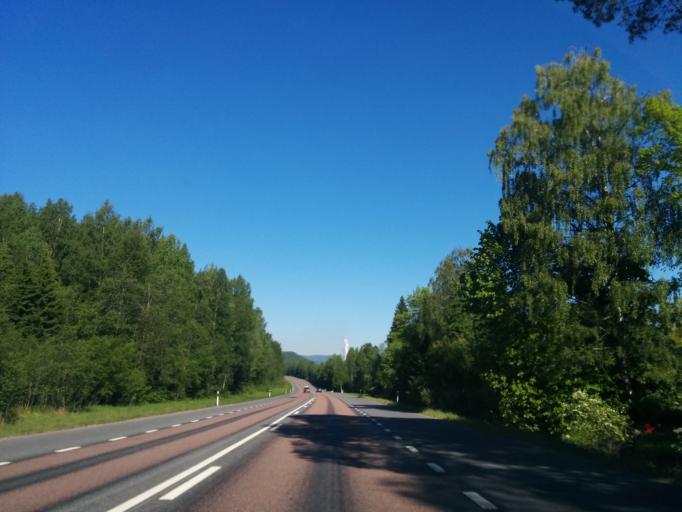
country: SE
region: Vaesternorrland
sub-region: Kramfors Kommun
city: Kramfors
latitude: 62.9548
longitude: 17.7639
